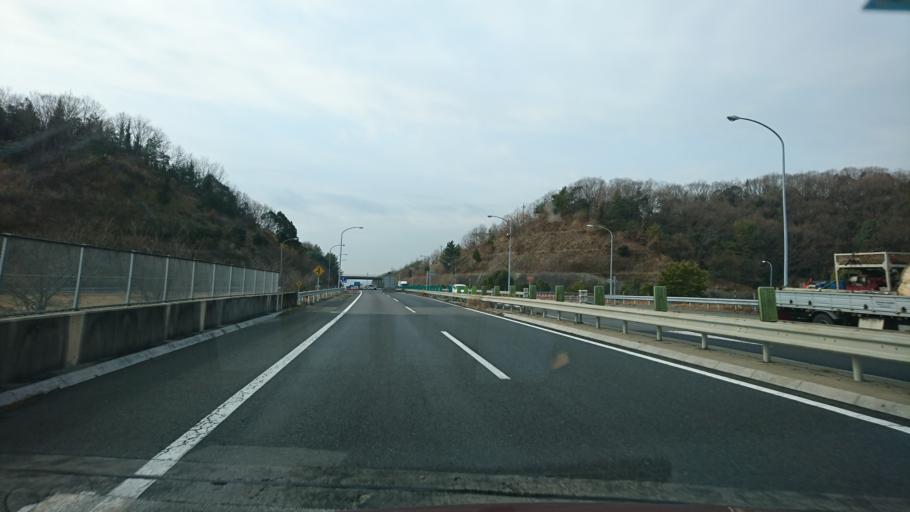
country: JP
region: Okayama
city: Okayama-shi
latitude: 34.7020
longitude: 133.8875
